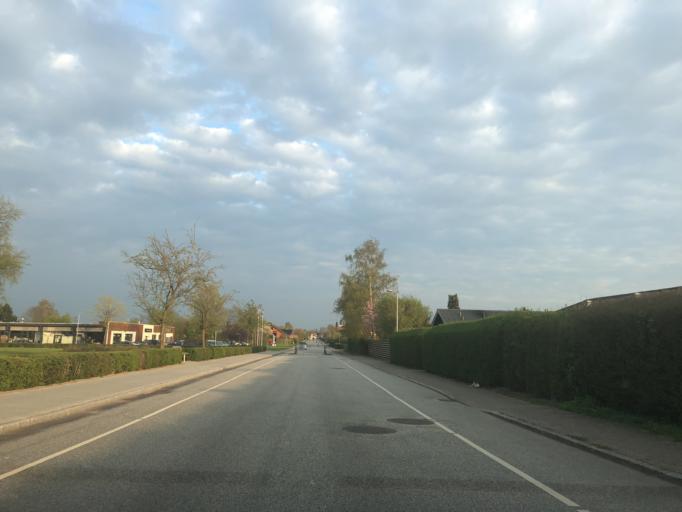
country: DK
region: Zealand
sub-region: Ringsted Kommune
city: Ringsted
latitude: 55.4630
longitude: 11.7884
